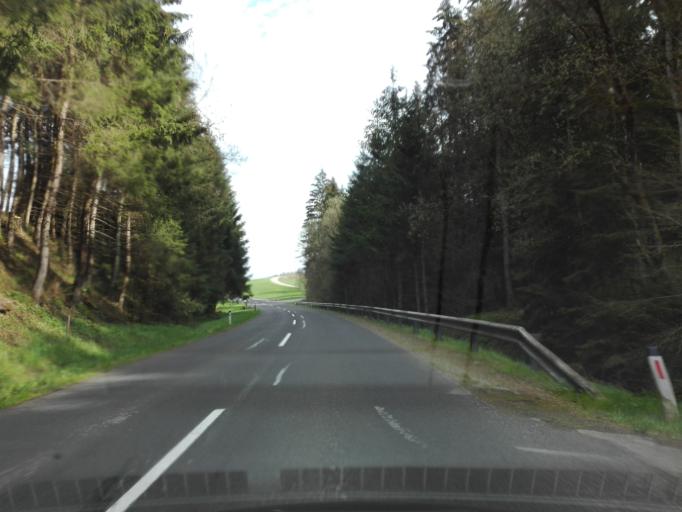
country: AT
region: Upper Austria
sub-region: Politischer Bezirk Rohrbach
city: Kleinzell im Muehlkreis
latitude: 48.4718
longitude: 14.0140
